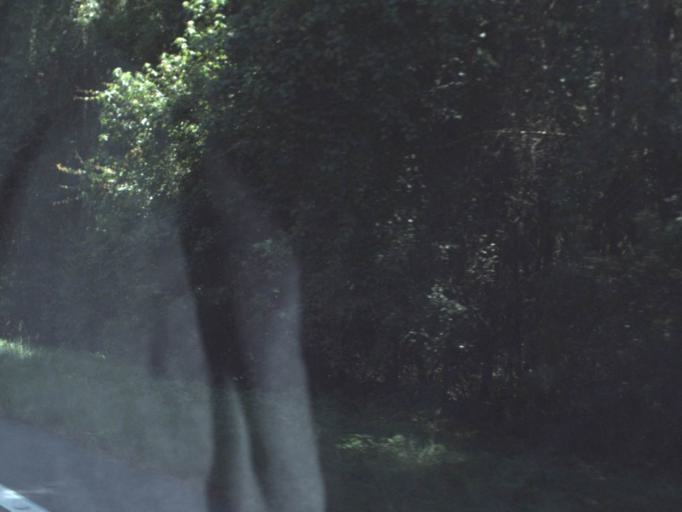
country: US
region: Florida
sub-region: Nassau County
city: Yulee
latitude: 30.6925
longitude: -81.6574
